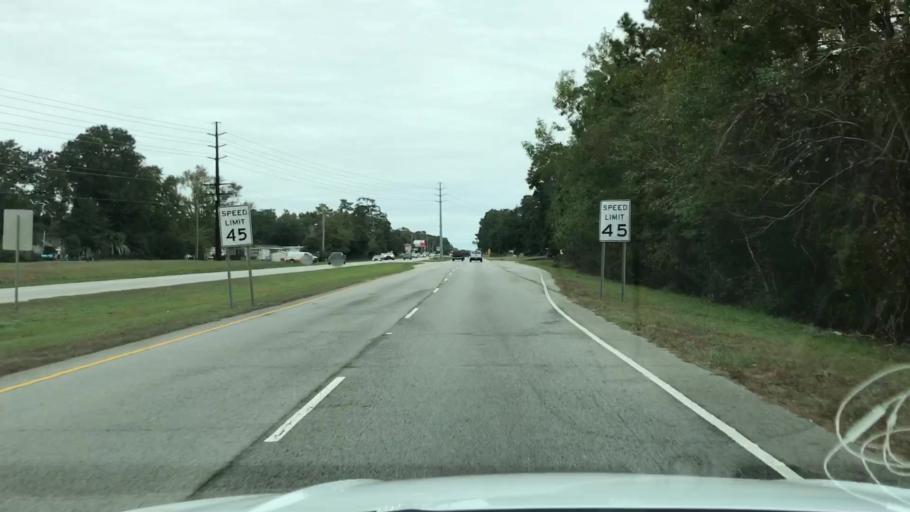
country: US
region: South Carolina
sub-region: Georgetown County
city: Murrells Inlet
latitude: 33.5309
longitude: -79.0610
